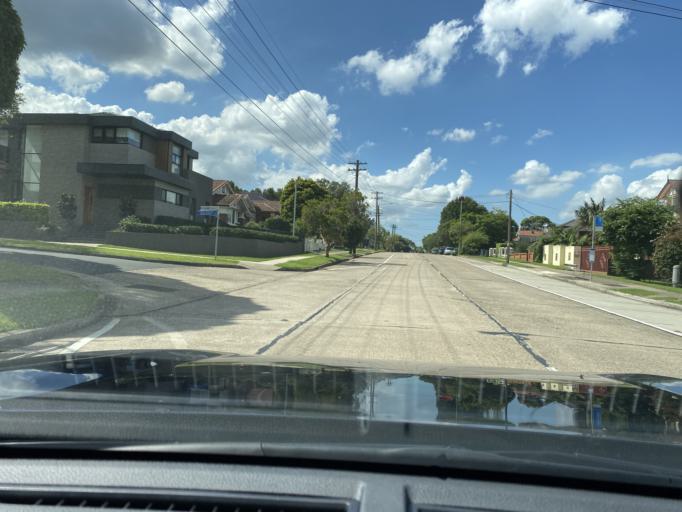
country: AU
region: New South Wales
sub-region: Canada Bay
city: Concord
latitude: -33.8512
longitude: 151.1106
